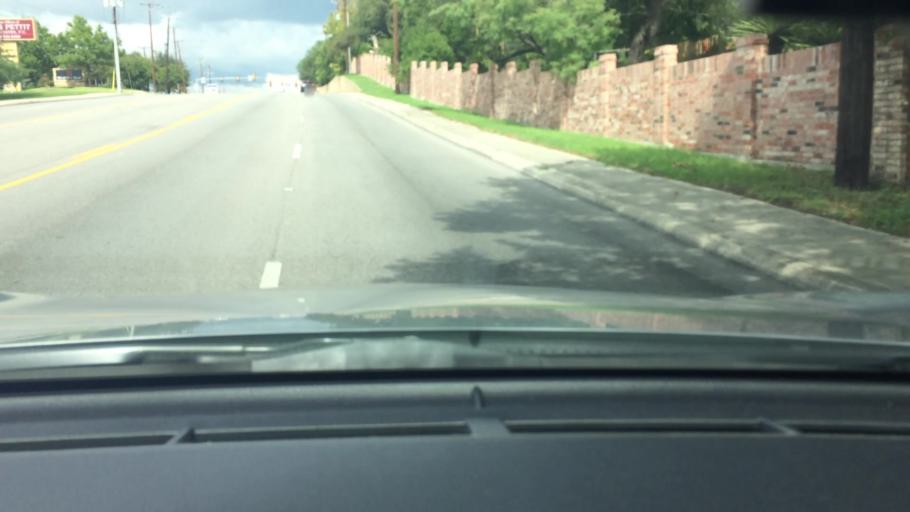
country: US
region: Texas
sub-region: Bexar County
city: Shavano Park
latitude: 29.5629
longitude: -98.5595
